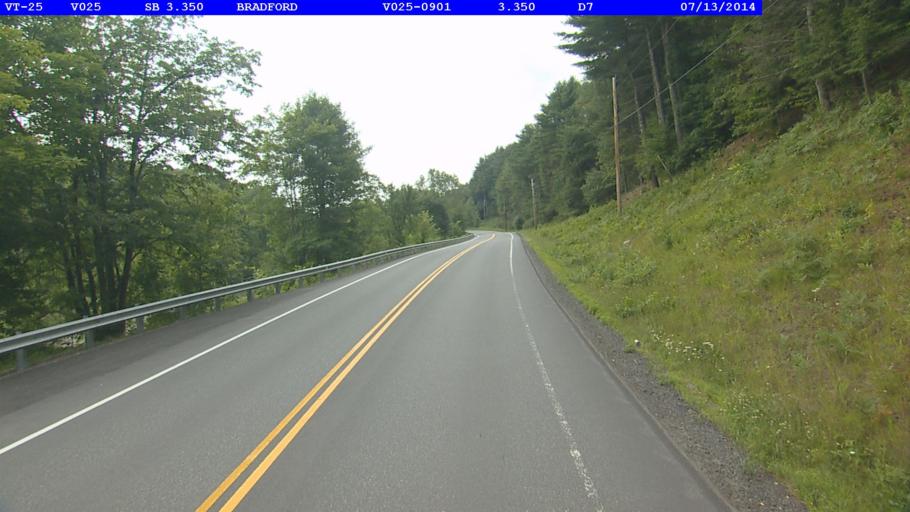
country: US
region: New Hampshire
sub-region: Grafton County
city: Orford
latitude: 44.0030
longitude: -72.1624
